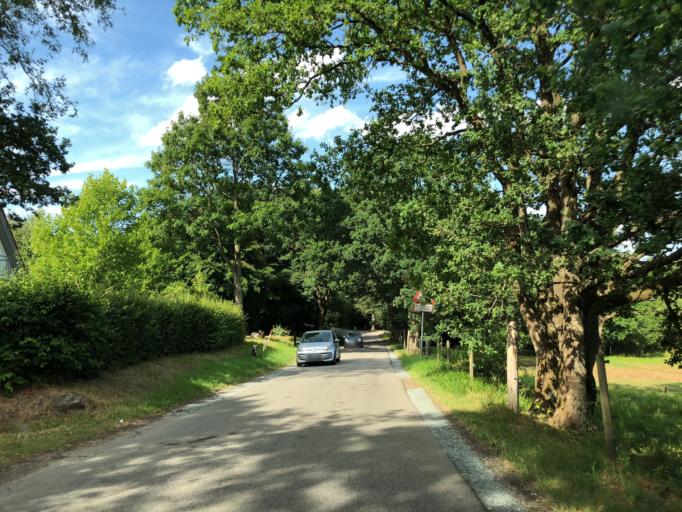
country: DK
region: South Denmark
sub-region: Vejle Kommune
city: Egtved
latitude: 55.6606
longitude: 9.3032
